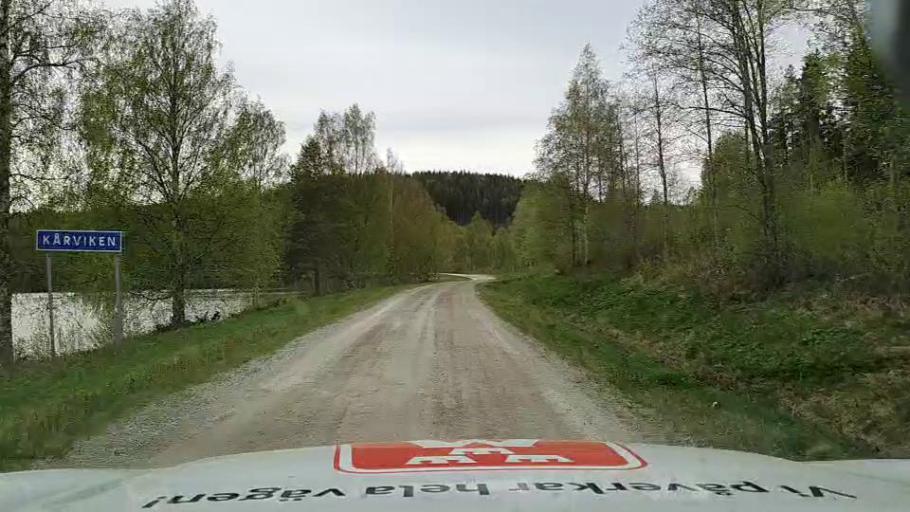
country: SE
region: Jaemtland
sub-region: Bergs Kommun
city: Hoverberg
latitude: 62.6886
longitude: 14.7814
